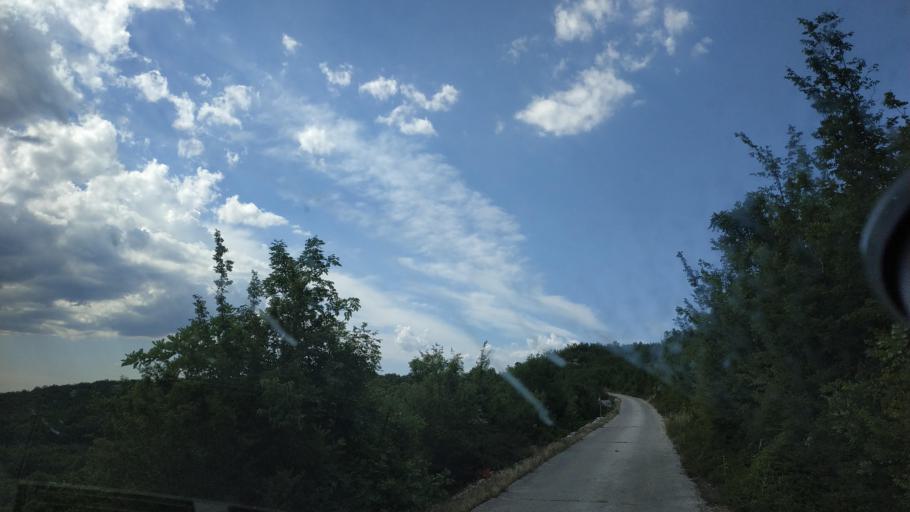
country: HR
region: Splitsko-Dalmatinska
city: Dugopolje
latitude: 43.5653
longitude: 16.6545
